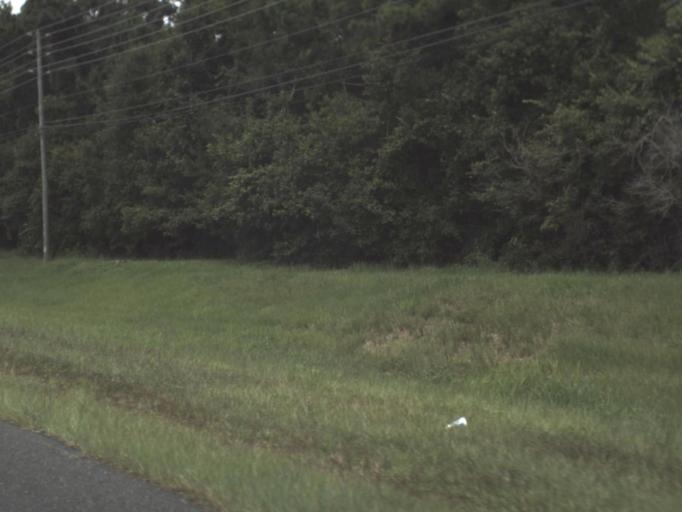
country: US
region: Florida
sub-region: Hernando County
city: South Brooksville
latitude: 28.5073
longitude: -82.4218
